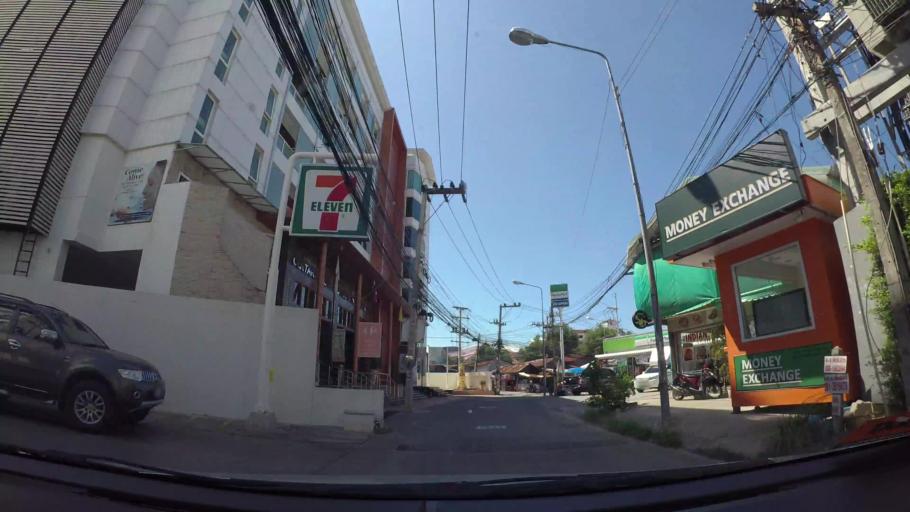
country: TH
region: Chon Buri
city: Phatthaya
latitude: 12.9386
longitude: 100.8906
